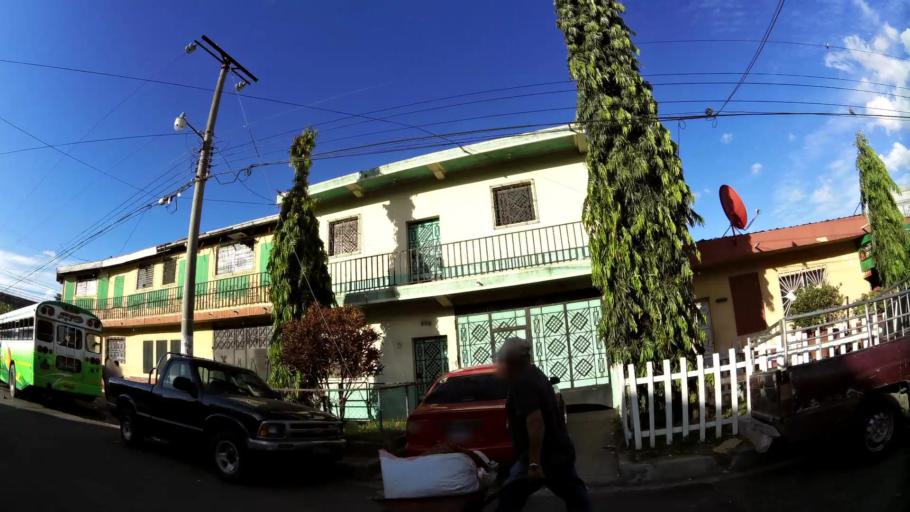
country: SV
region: Cuscatlan
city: Cojutepeque
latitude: 13.7178
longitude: -88.9324
